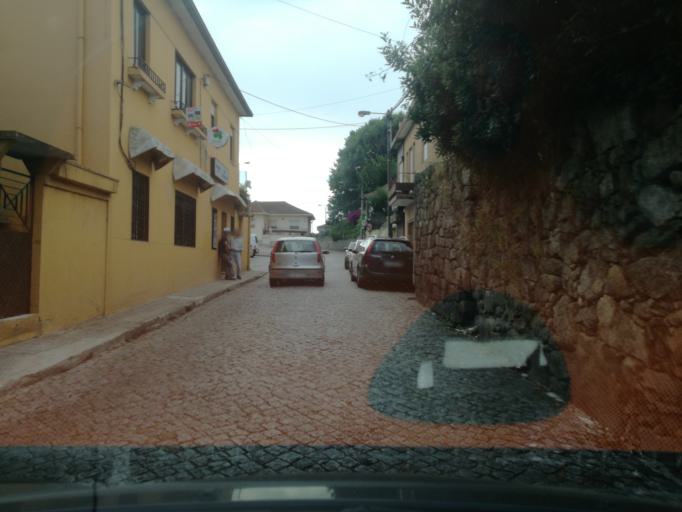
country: PT
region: Porto
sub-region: Maia
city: Maia
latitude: 41.2453
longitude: -8.6050
